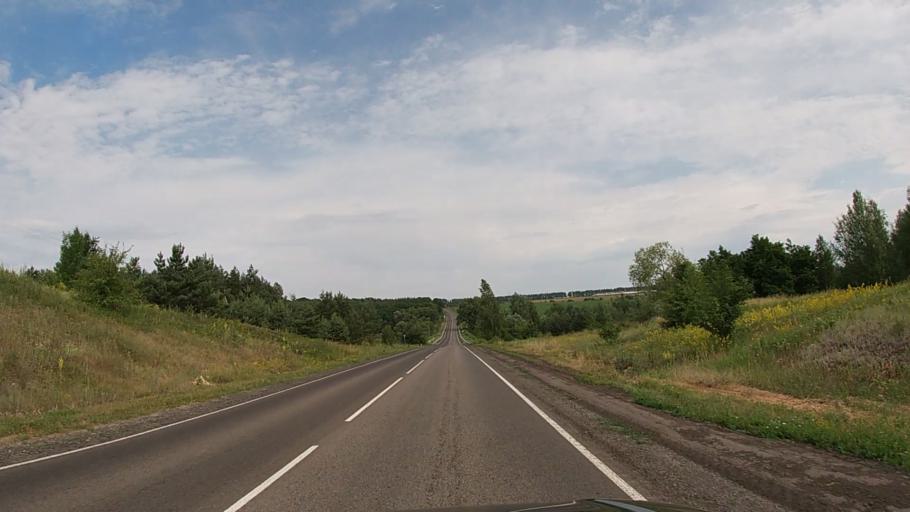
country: RU
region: Belgorod
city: Krasnaya Yaruga
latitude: 50.8254
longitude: 35.4988
